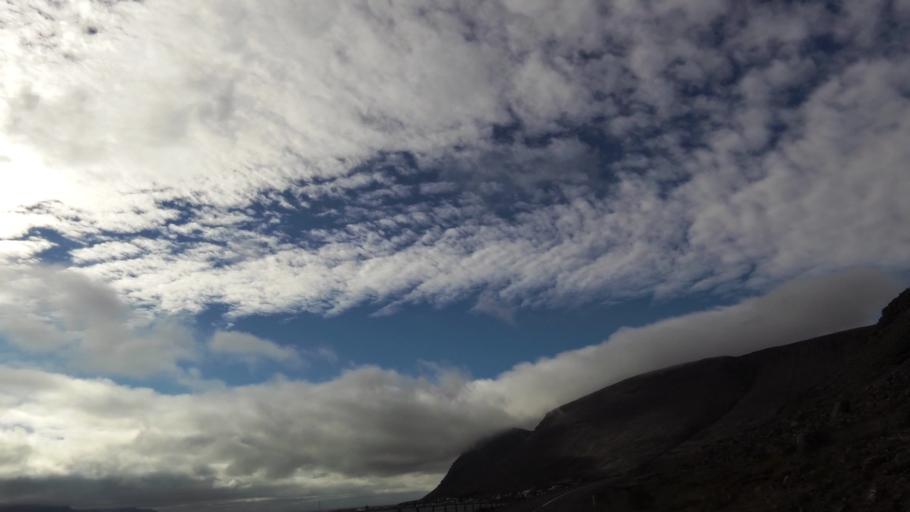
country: IS
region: West
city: Olafsvik
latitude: 65.5843
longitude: -23.9671
